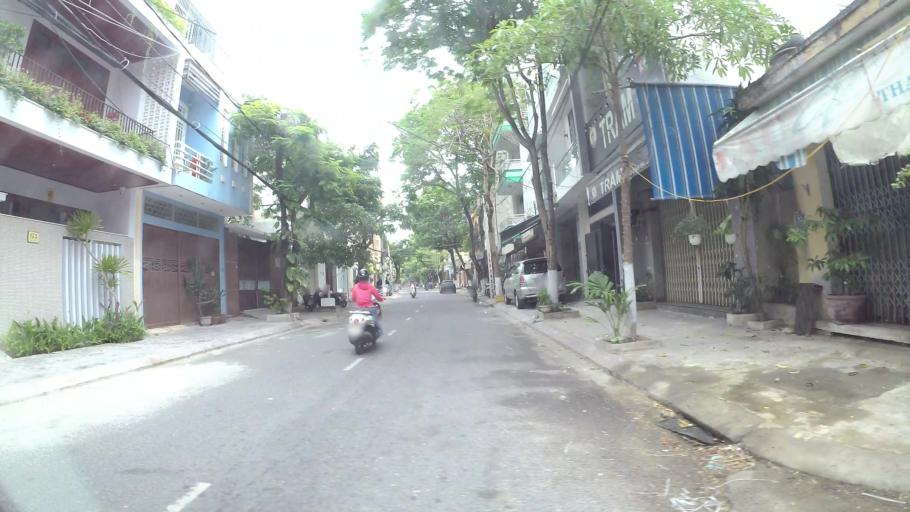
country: VN
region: Da Nang
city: Da Nang
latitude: 16.0815
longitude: 108.2135
